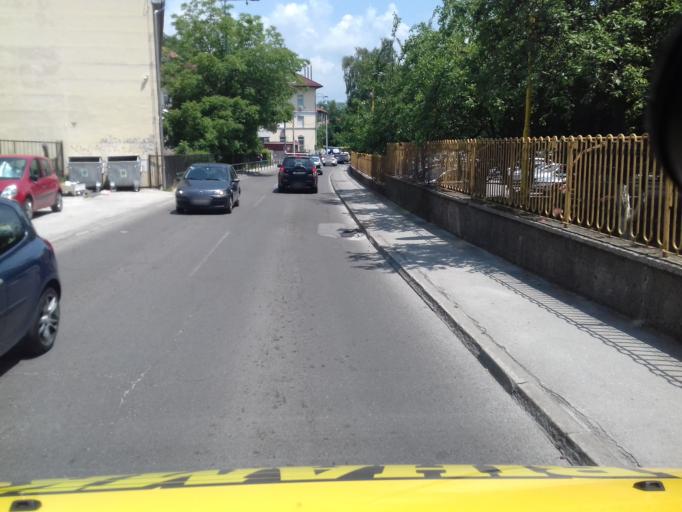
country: BA
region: Federation of Bosnia and Herzegovina
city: Kobilja Glava
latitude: 43.8594
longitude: 18.3888
